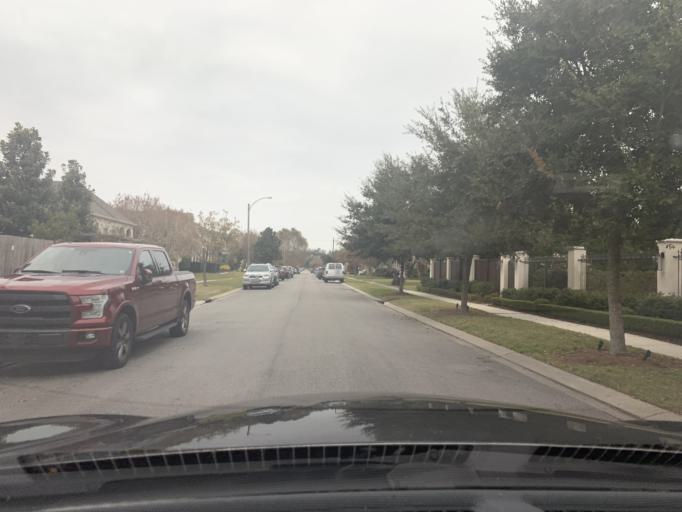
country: US
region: Louisiana
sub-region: Jefferson Parish
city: Metairie
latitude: 30.0123
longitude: -90.1059
